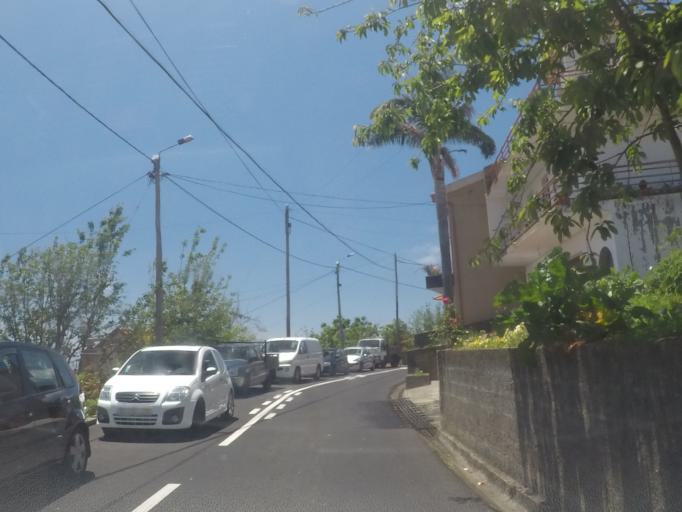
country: PT
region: Madeira
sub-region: Camara de Lobos
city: Curral das Freiras
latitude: 32.6854
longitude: -16.9954
